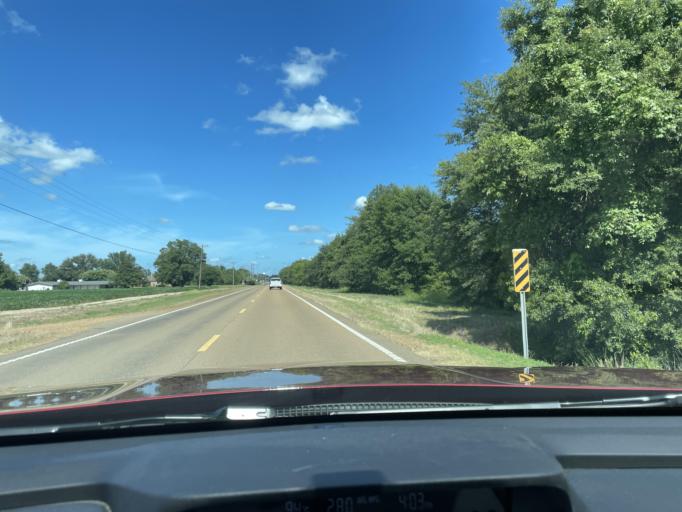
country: US
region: Mississippi
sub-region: Humphreys County
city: Belzoni
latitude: 33.1838
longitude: -90.5059
